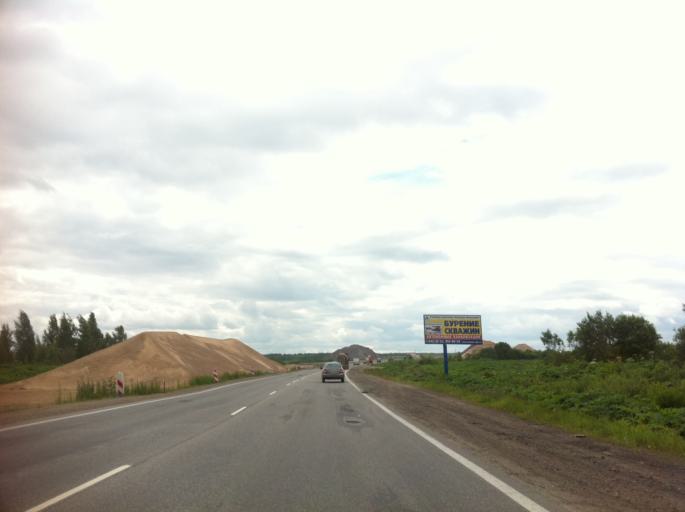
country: RU
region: Leningrad
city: Gatchina
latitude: 59.5458
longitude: 30.1643
